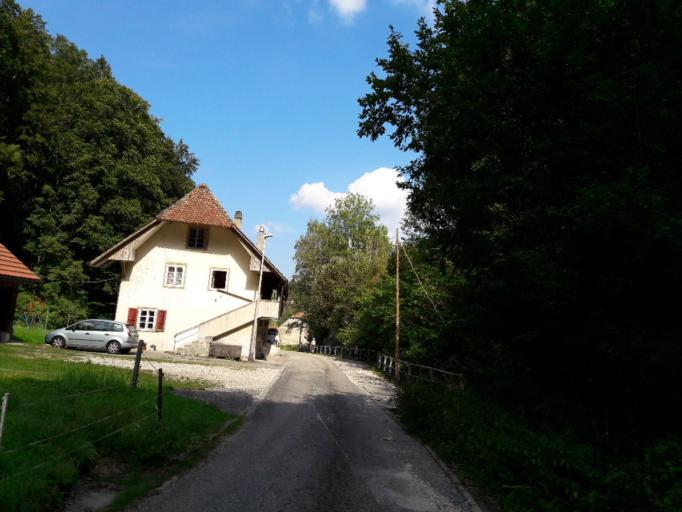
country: CH
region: Solothurn
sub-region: Bezirk Lebern
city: Selzach
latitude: 47.2609
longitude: 7.4652
